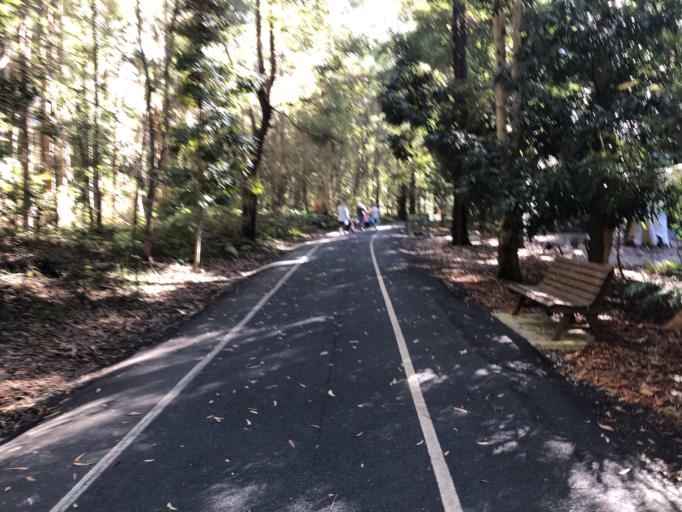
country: AU
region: New South Wales
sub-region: Coffs Harbour
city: Coffs Harbour
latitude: -30.2967
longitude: 153.1249
